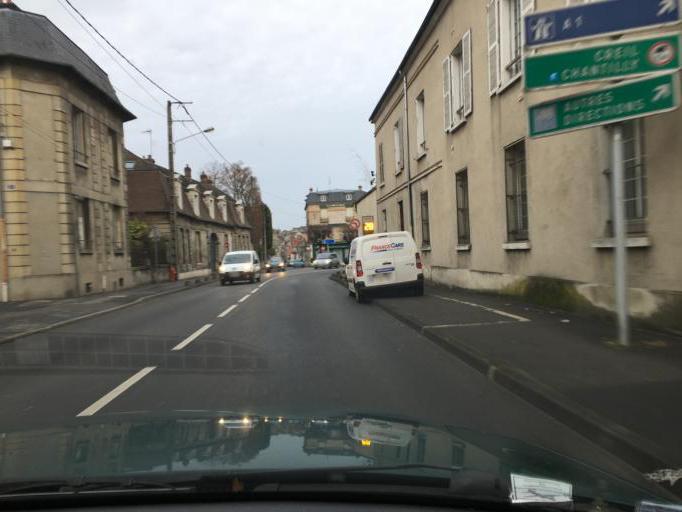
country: FR
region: Picardie
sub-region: Departement de l'Oise
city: Senlis
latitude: 49.2002
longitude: 2.5802
